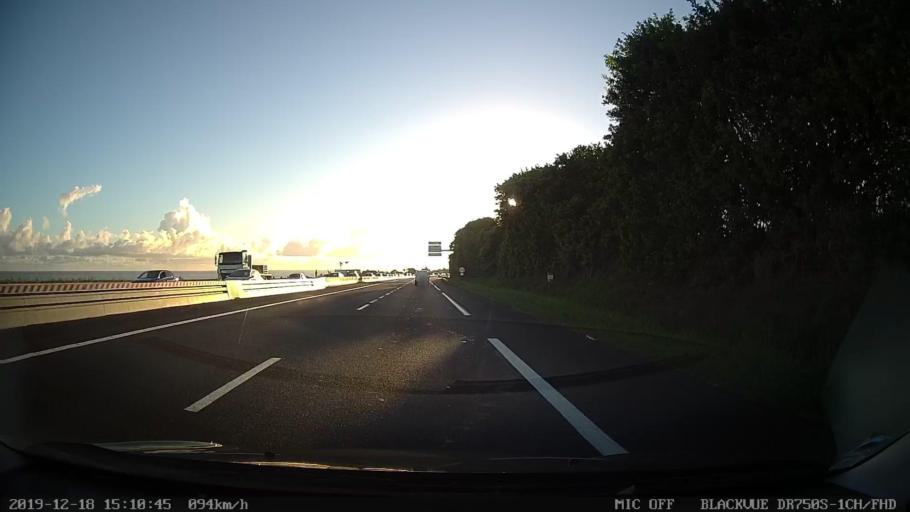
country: RE
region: Reunion
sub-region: Reunion
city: Sainte-Suzanne
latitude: -20.9016
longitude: 55.5917
